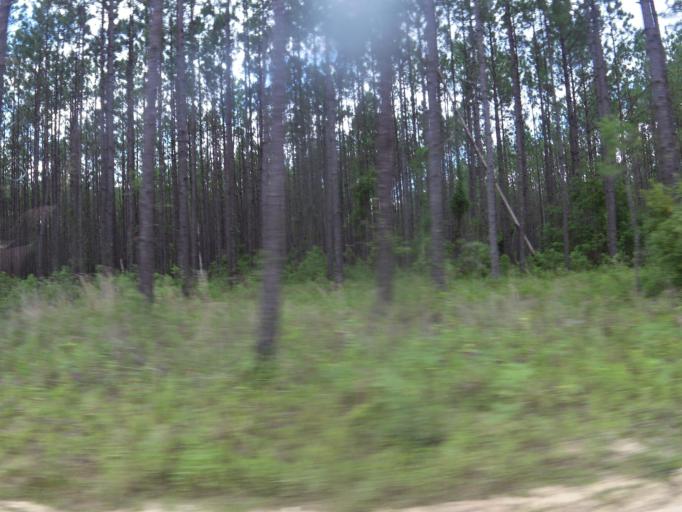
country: US
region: Florida
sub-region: Clay County
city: Asbury Lake
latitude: 29.9052
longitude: -81.8142
